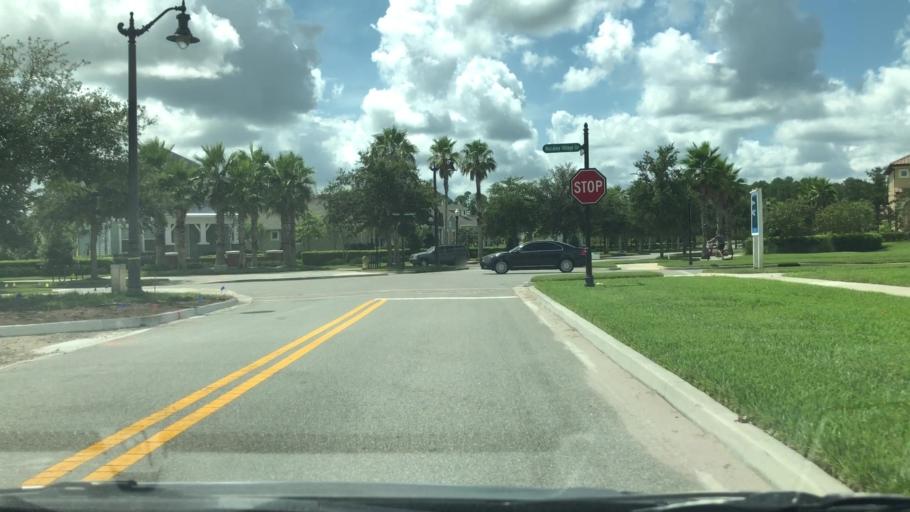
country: US
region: Florida
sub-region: Saint Johns County
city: Palm Valley
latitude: 30.1086
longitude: -81.4208
